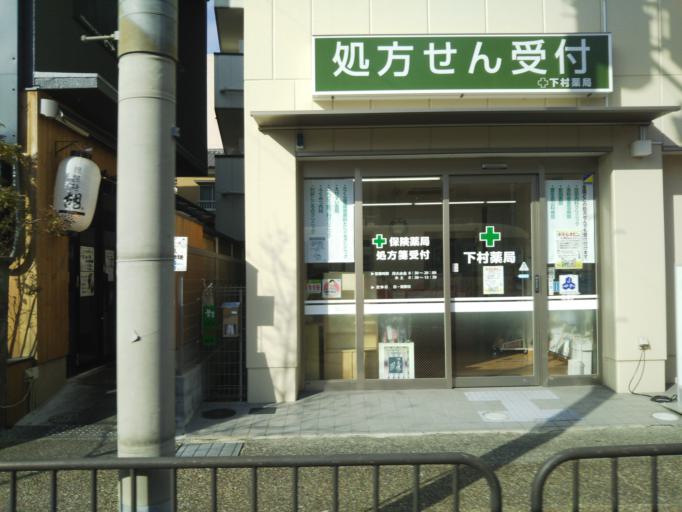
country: JP
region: Shiga Prefecture
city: Otsu-shi
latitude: 34.9892
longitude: 135.8124
